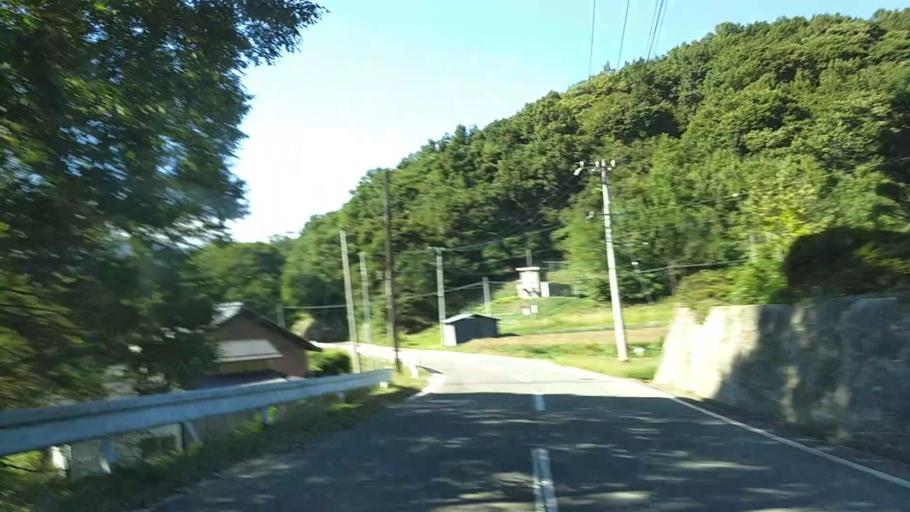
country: JP
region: Nagano
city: Nagano-shi
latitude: 36.6057
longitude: 138.0926
